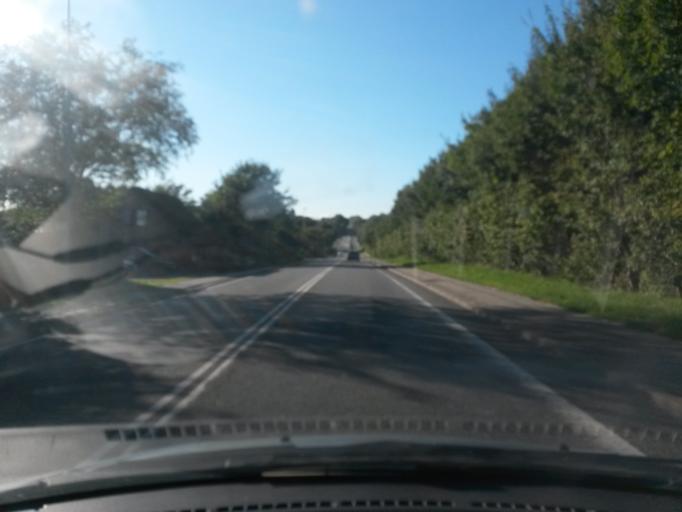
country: DK
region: Central Jutland
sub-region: Arhus Kommune
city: Sabro
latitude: 56.2244
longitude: 9.9654
